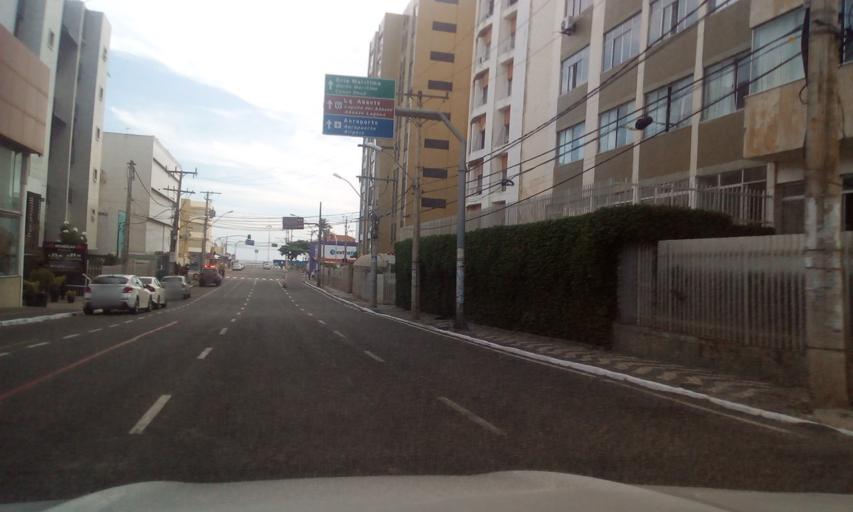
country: BR
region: Bahia
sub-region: Salvador
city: Salvador
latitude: -13.0043
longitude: -38.4589
